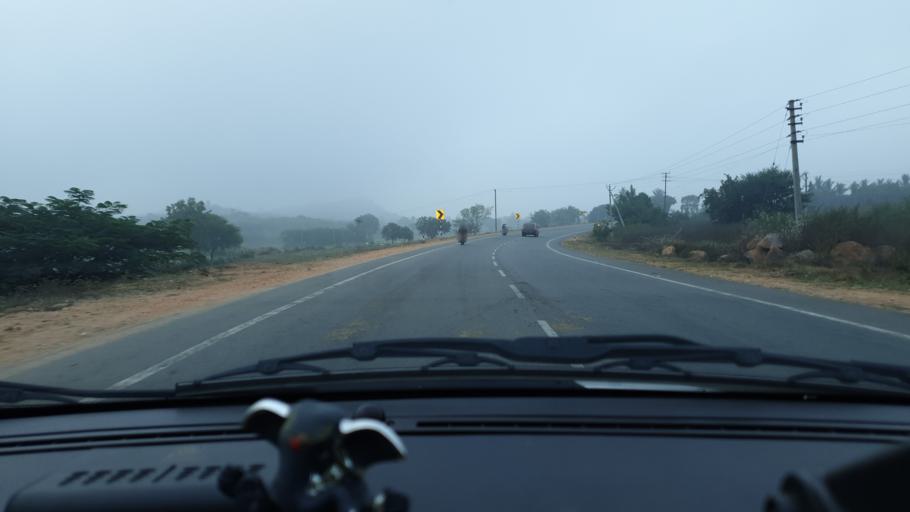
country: IN
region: Telangana
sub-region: Mahbubnagar
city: Farrukhnagar
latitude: 16.9373
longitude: 78.5284
